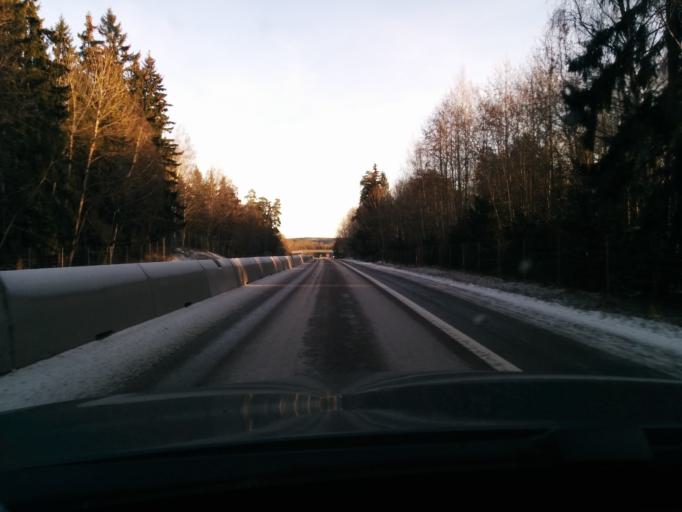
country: SE
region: Stockholm
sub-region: Upplands Vasby Kommun
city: Upplands Vaesby
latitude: 59.4748
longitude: 17.8745
